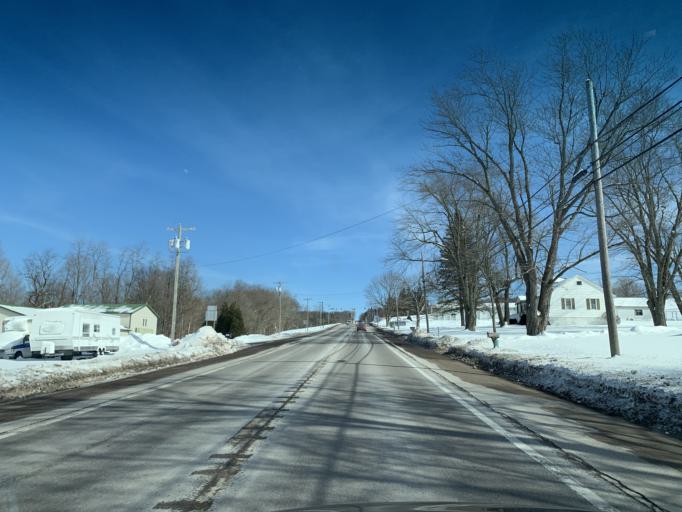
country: US
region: Pennsylvania
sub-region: Somerset County
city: Meyersdale
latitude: 39.6956
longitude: -79.1209
